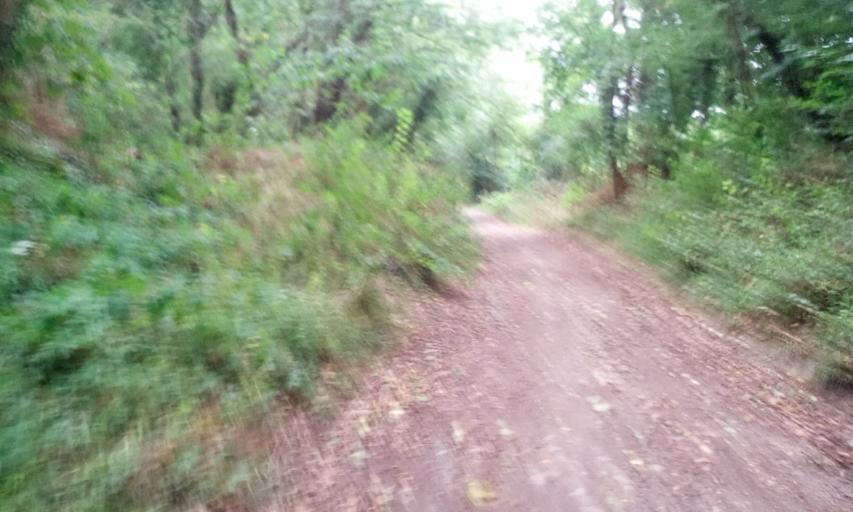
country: FR
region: Lower Normandy
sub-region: Departement du Calvados
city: Fontaine-Etoupefour
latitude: 49.1458
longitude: -0.4666
